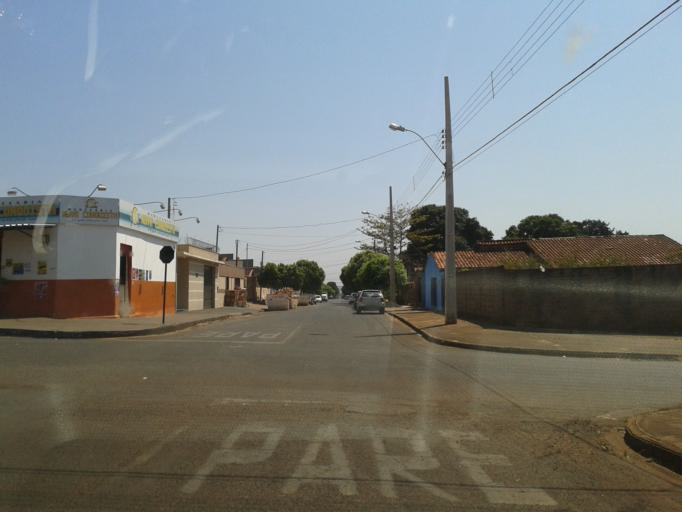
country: BR
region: Minas Gerais
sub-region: Ituiutaba
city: Ituiutaba
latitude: -18.9892
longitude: -49.4460
